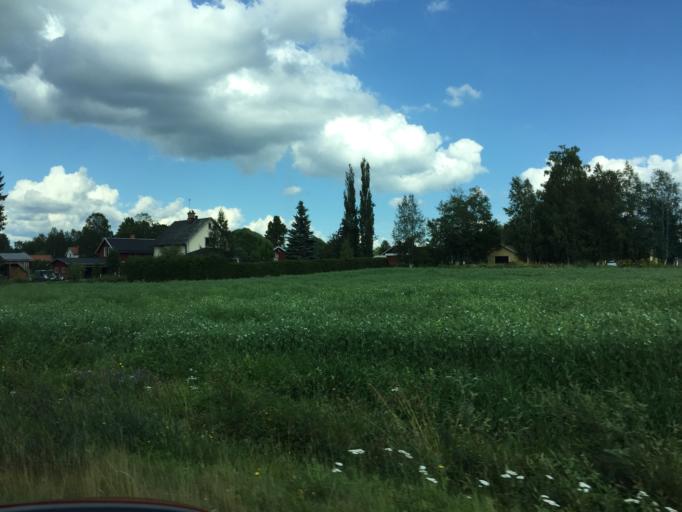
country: SE
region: Gaevleborg
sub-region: Bollnas Kommun
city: Arbra
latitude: 61.5225
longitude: 16.3639
